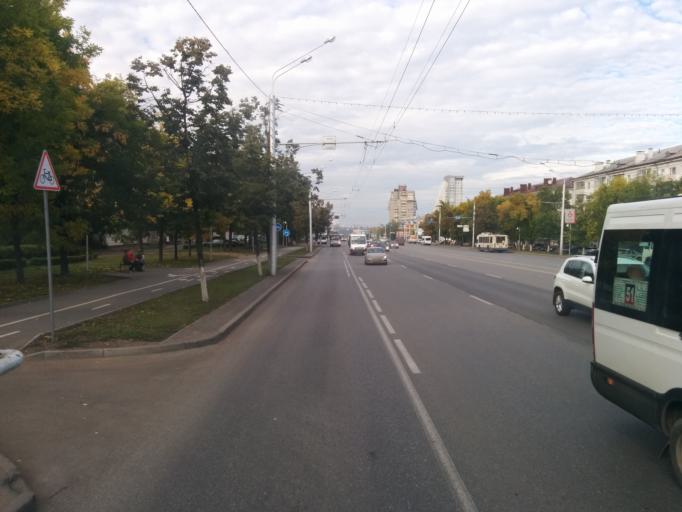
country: RU
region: Bashkortostan
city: Ufa
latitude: 54.7800
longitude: 56.0313
